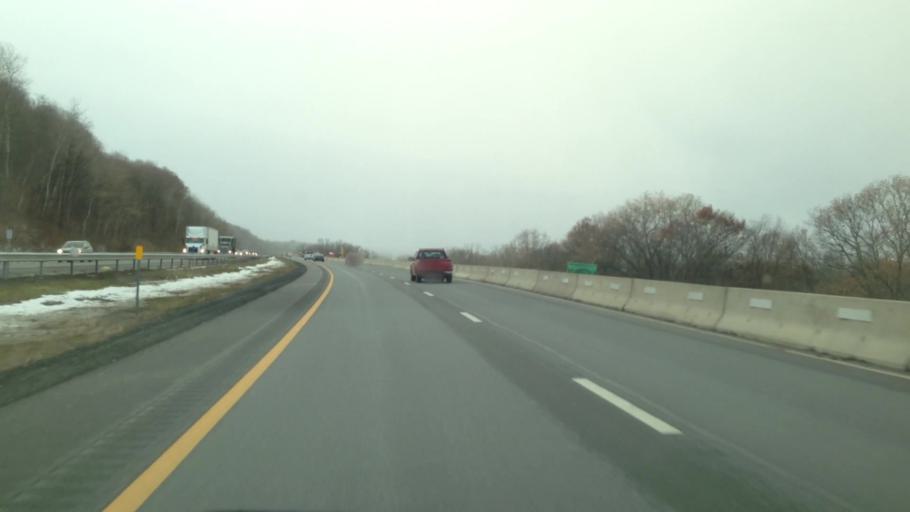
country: US
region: New York
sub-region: Schenectady County
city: Scotia
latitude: 42.8717
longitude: -74.0496
